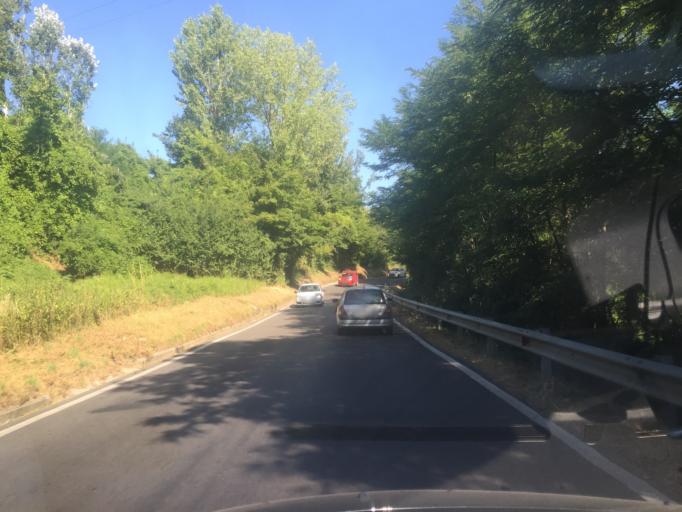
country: IT
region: Tuscany
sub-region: Provincia di Lucca
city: Castelnuovo di Garfagnana
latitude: 44.1221
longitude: 10.3928
